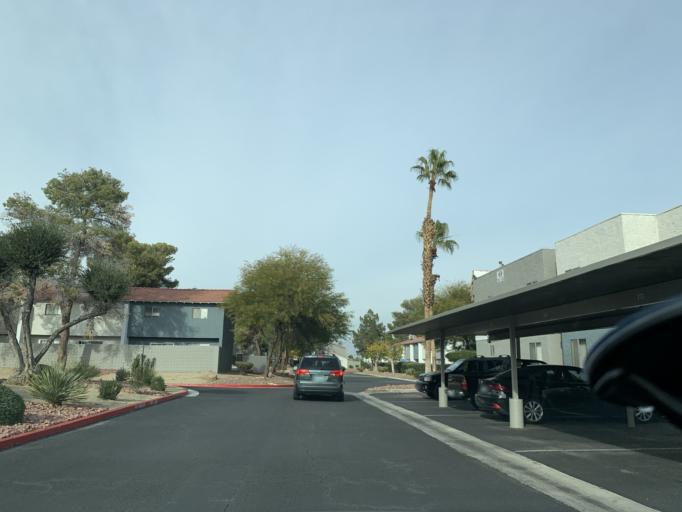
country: US
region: Nevada
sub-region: Clark County
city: Spring Valley
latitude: 36.0980
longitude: -115.2297
